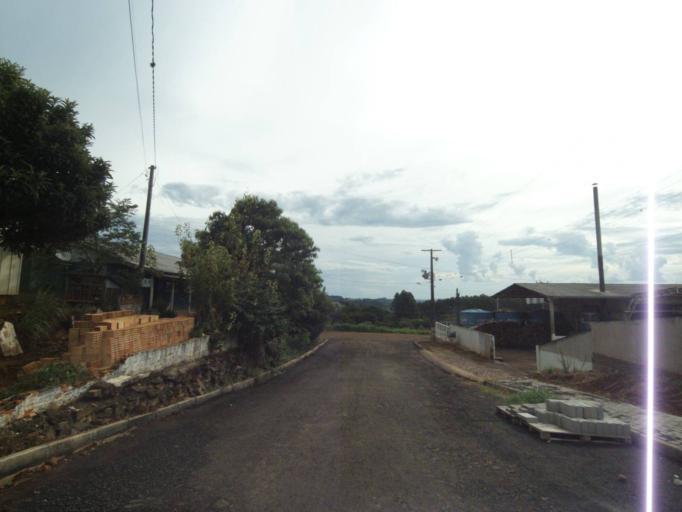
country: BR
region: Parana
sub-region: Guaraniacu
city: Guaraniacu
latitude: -25.1033
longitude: -52.8774
